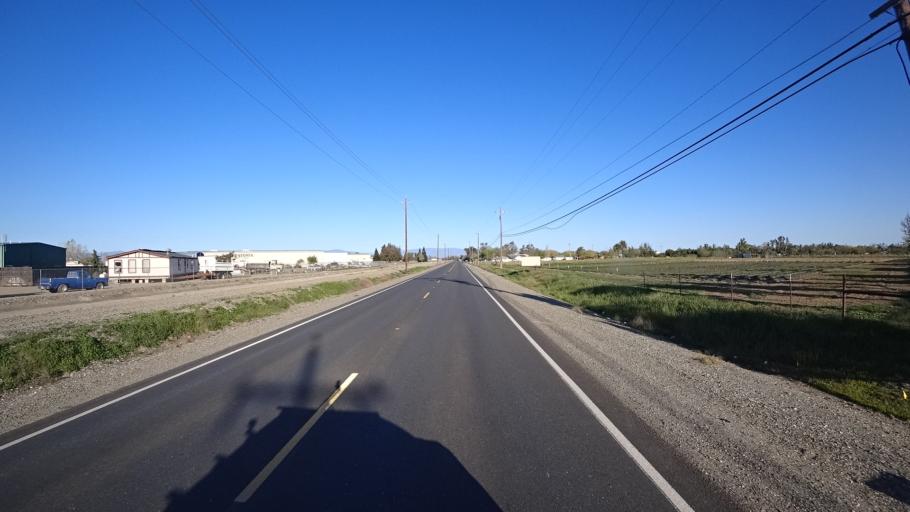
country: US
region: California
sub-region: Glenn County
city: Orland
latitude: 39.7558
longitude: -122.2180
